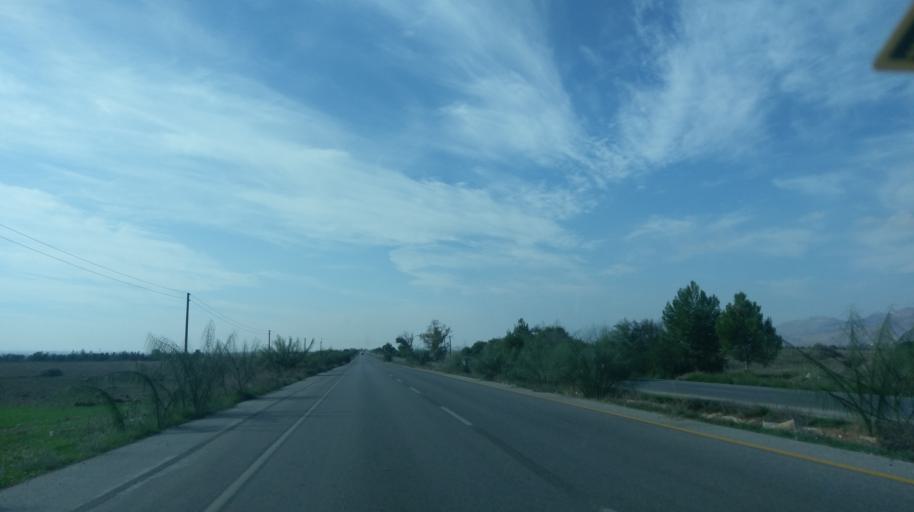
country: CY
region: Larnaka
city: Athienou
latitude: 35.2088
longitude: 33.5806
